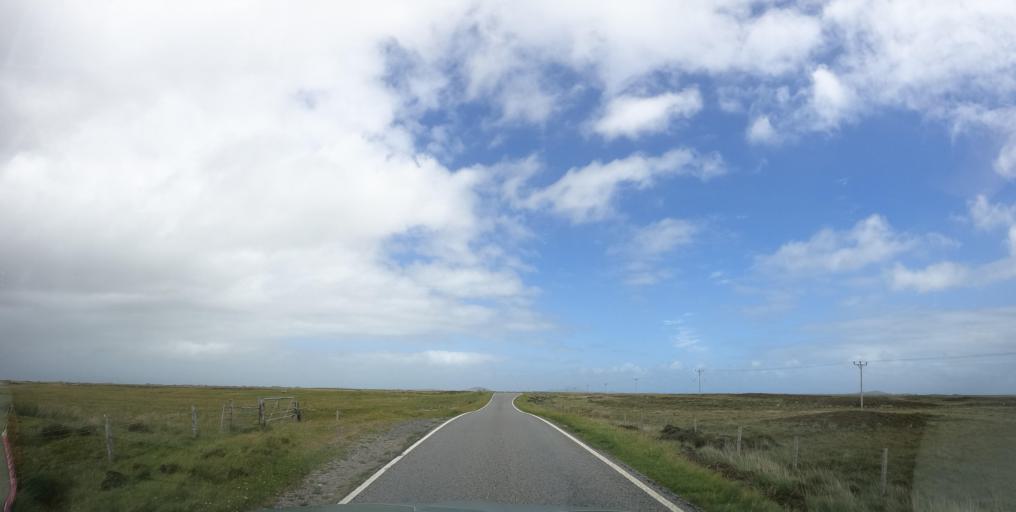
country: GB
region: Scotland
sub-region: Eilean Siar
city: Benbecula
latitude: 57.3678
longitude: -7.3509
